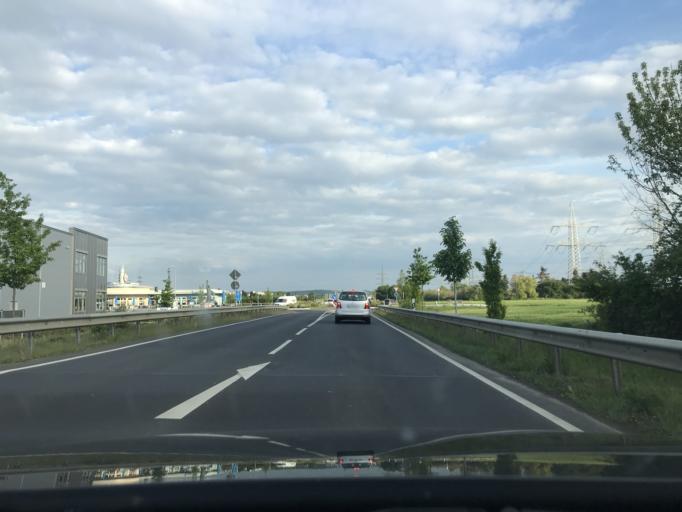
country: DE
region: North Rhine-Westphalia
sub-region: Regierungsbezirk Koln
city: Alfter
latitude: 50.7555
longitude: 7.0278
